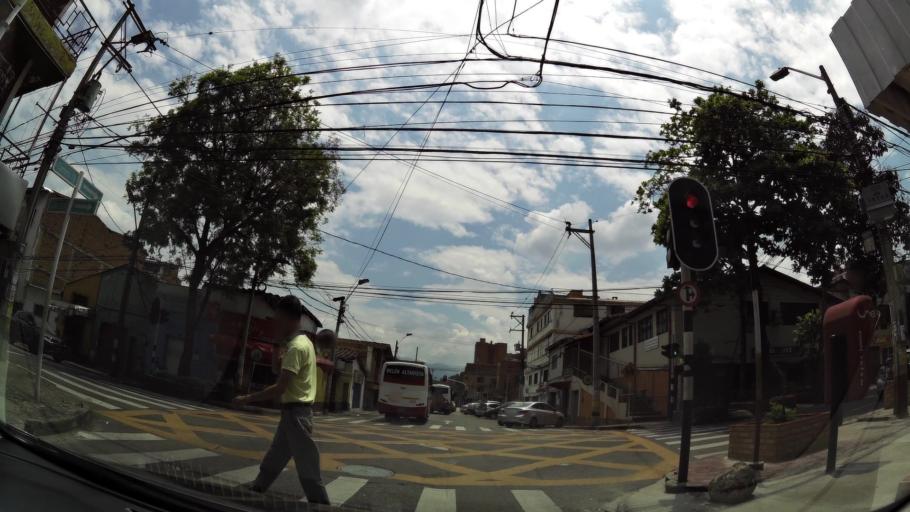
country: CO
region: Antioquia
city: Medellin
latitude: 6.2322
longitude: -75.5982
